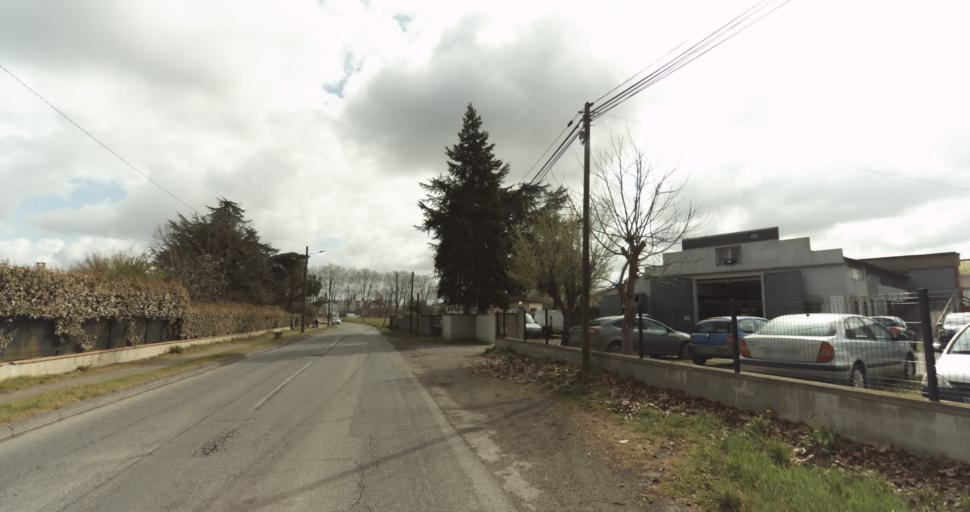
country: FR
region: Midi-Pyrenees
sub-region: Departement de la Haute-Garonne
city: Auterive
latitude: 43.3503
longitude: 1.4650
